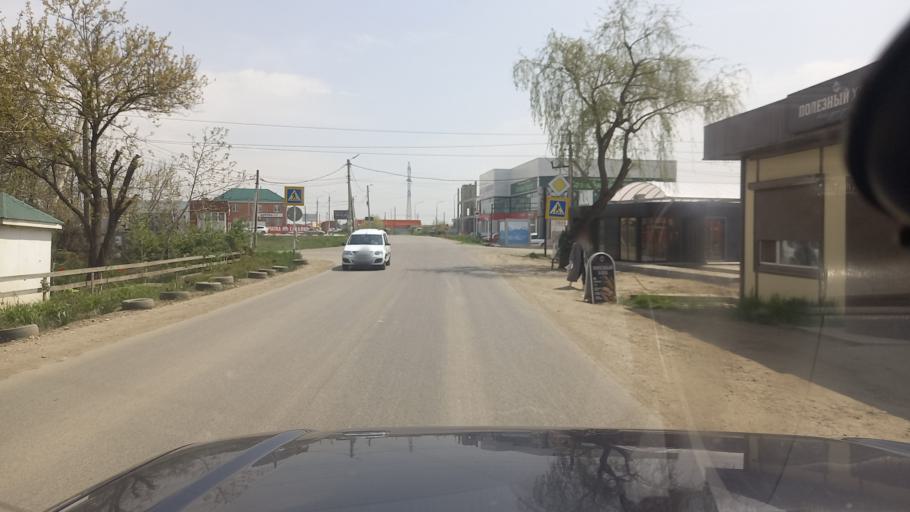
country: RU
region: Adygeya
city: Yablonovskiy
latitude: 44.9863
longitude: 38.9625
